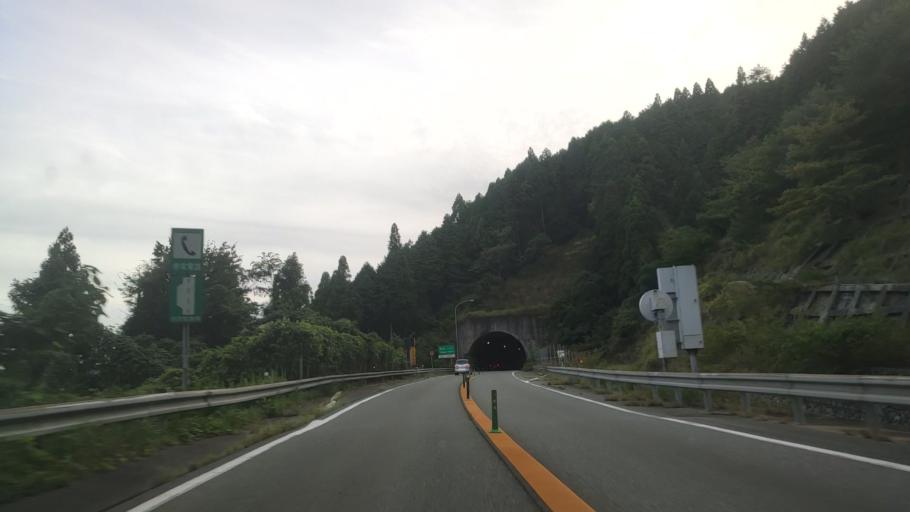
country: JP
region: Hyogo
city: Nishiwaki
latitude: 35.1658
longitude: 134.7897
